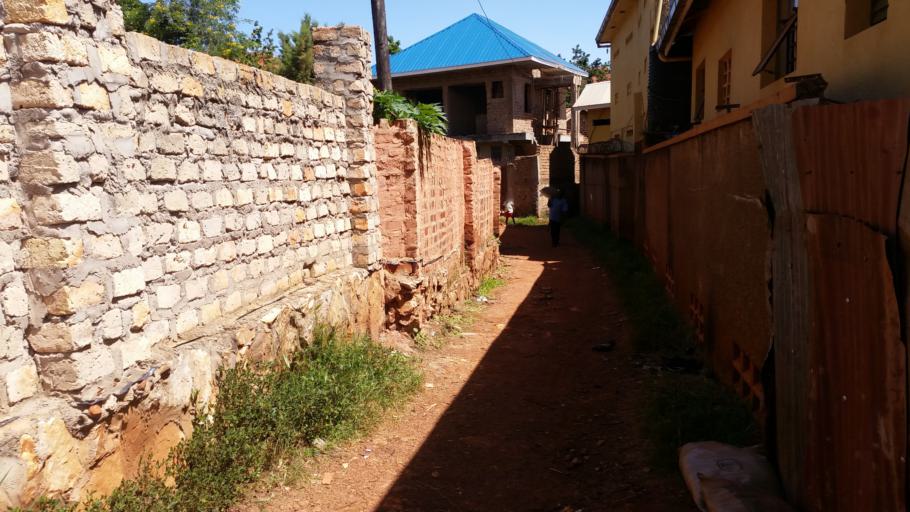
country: UG
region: Central Region
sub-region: Wakiso District
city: Kireka
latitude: 0.3393
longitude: 32.6479
